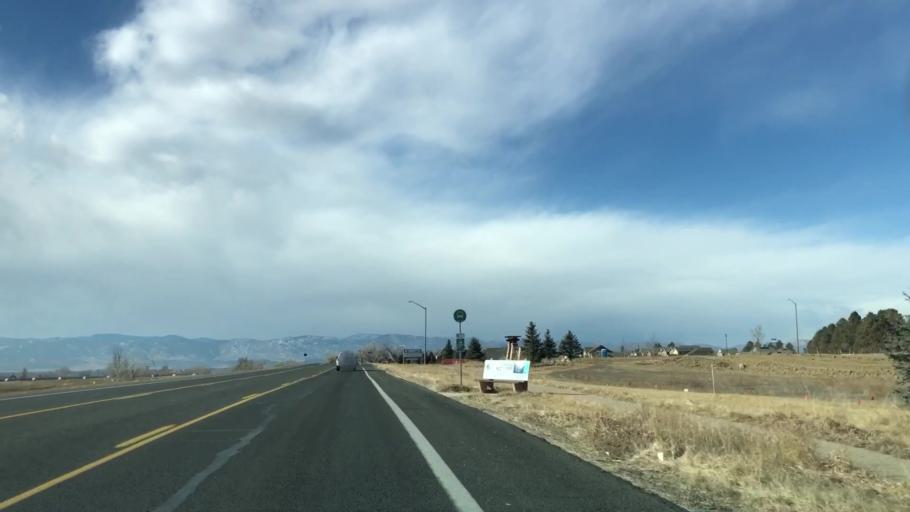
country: US
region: Colorado
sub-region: Larimer County
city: Fort Collins
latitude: 40.5958
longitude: -105.0122
